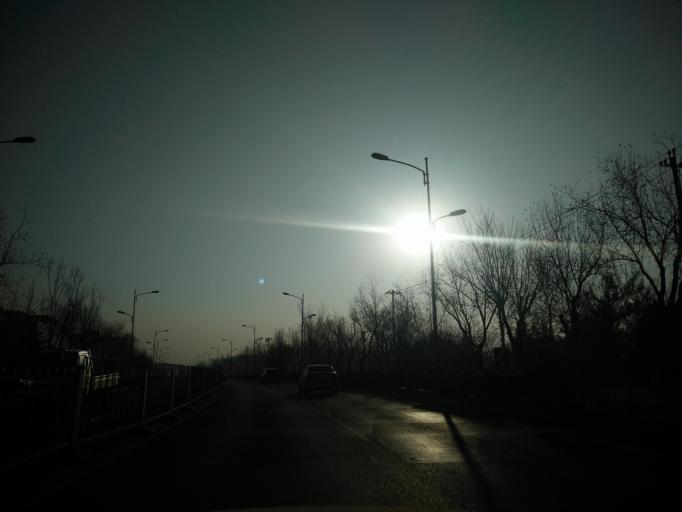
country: CN
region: Beijing
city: Jiugong
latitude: 39.7786
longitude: 116.4914
